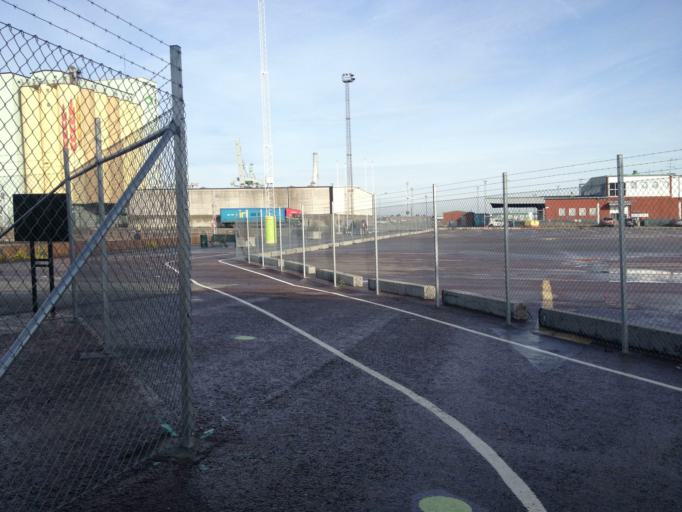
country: SE
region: Skane
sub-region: Malmo
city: Malmoe
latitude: 55.6137
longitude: 13.0030
